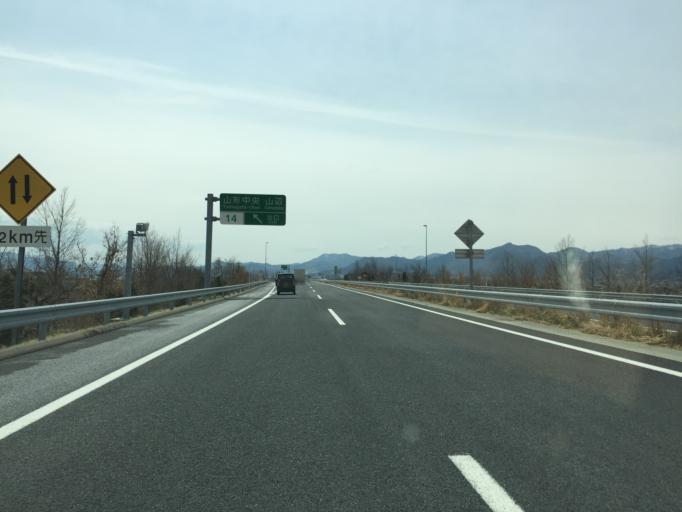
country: JP
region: Yamagata
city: Yamagata-shi
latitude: 38.2737
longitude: 140.2946
